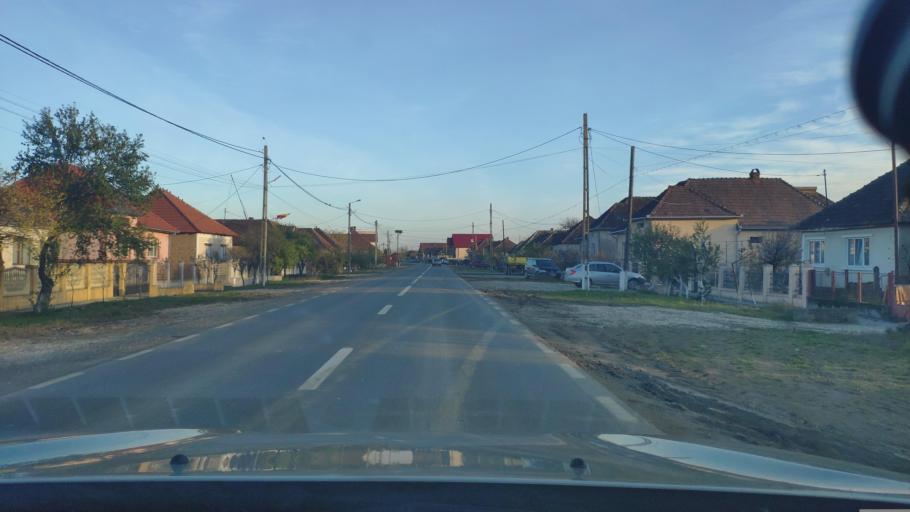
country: RO
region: Satu Mare
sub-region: Comuna Mediesu Aurit
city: Potau
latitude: 47.7750
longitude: 23.1000
